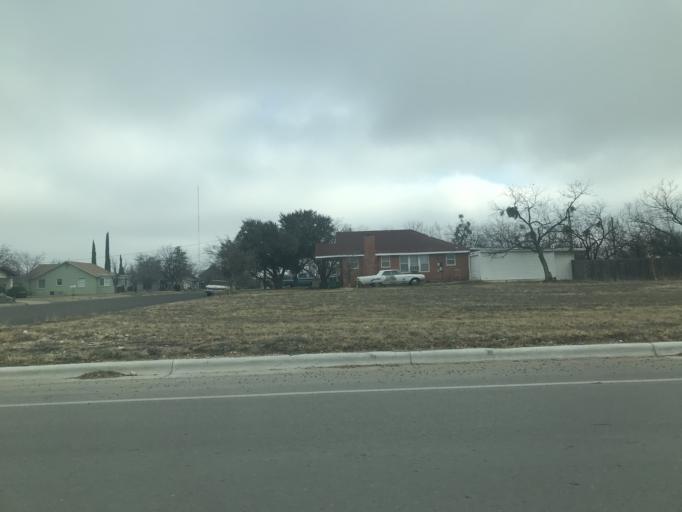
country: US
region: Texas
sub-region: Tom Green County
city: San Angelo
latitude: 31.4833
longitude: -100.4553
